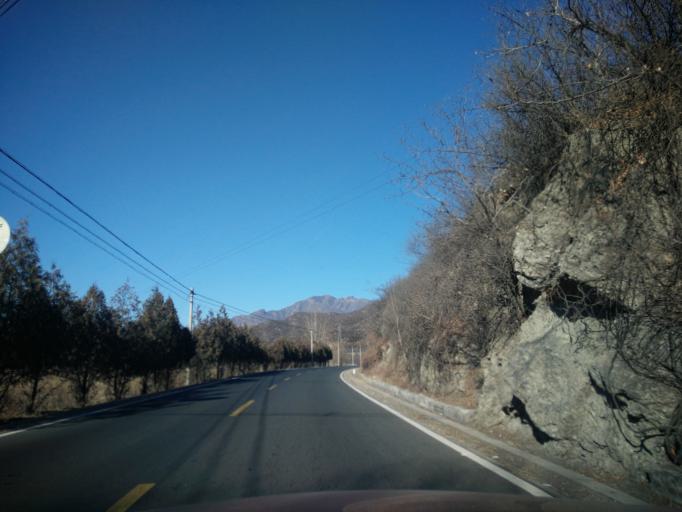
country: CN
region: Beijing
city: Zhaitang
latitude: 39.9846
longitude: 115.7427
